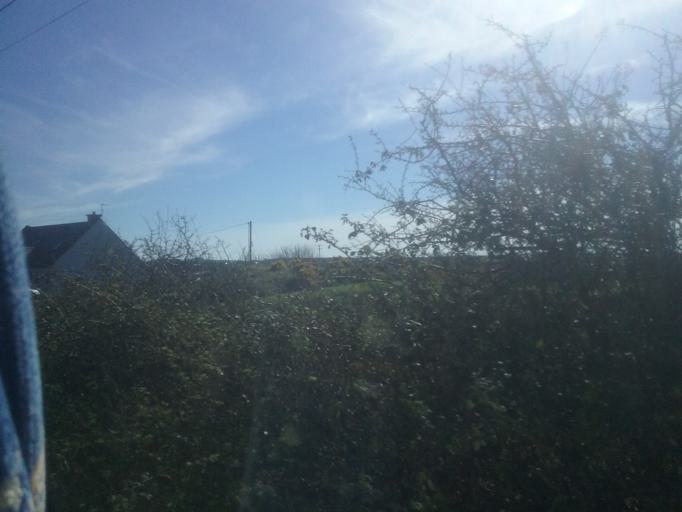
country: IE
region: Munster
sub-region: An Clar
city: Kilrush
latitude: 52.6699
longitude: -9.5193
